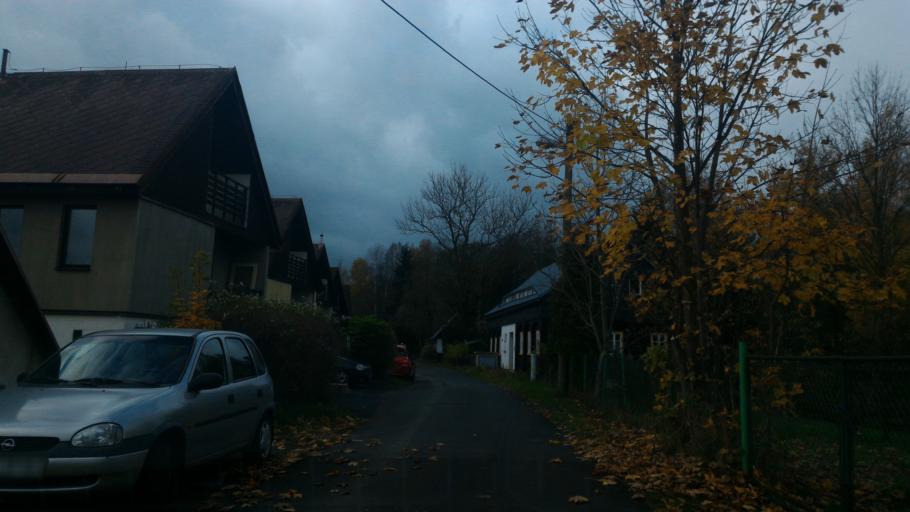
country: CZ
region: Ustecky
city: Dolni Podluzi
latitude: 50.8818
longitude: 14.5507
